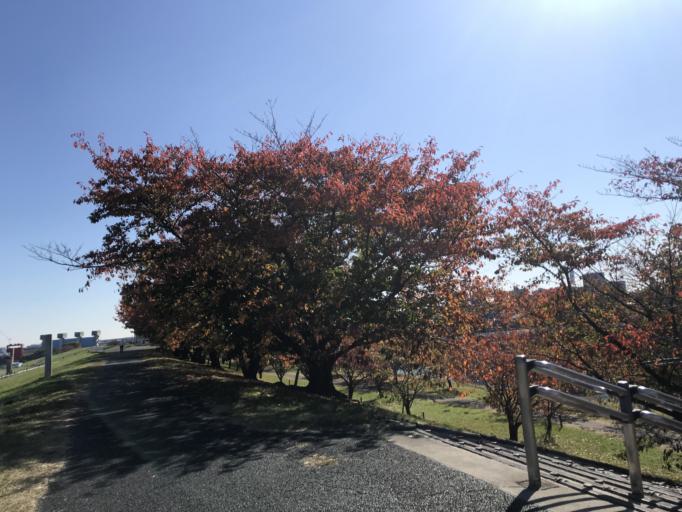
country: JP
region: Saitama
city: Kawaguchi
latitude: 35.7877
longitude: 139.7244
